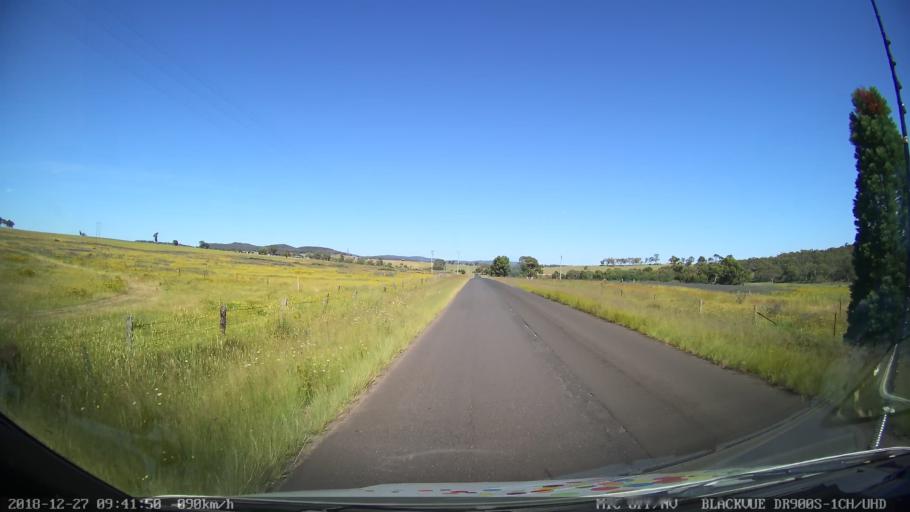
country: AU
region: New South Wales
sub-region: Lithgow
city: Portland
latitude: -33.3008
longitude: 150.0167
